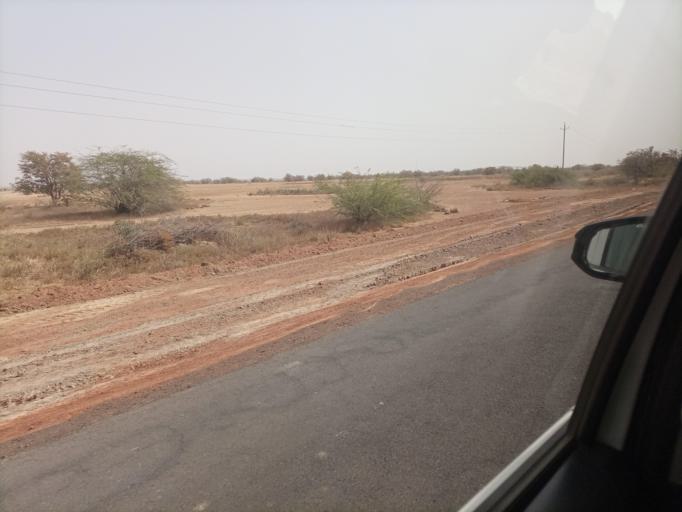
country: SN
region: Fatick
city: Foundiougne
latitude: 14.1647
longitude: -16.4646
